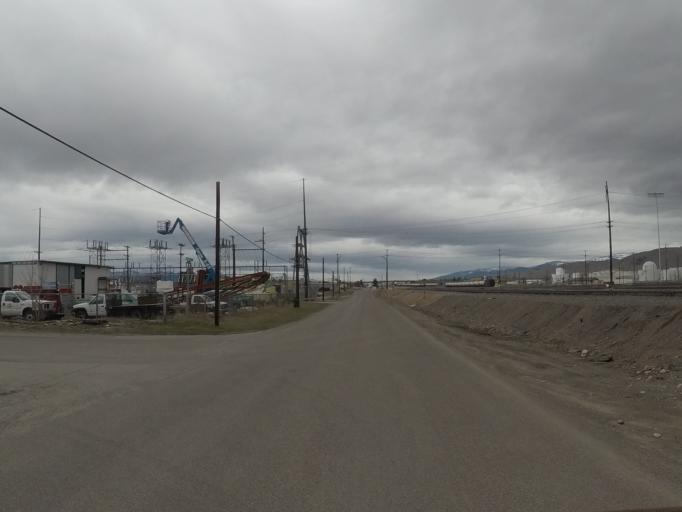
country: US
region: Montana
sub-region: Missoula County
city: Orchard Homes
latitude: 46.8924
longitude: -114.0265
